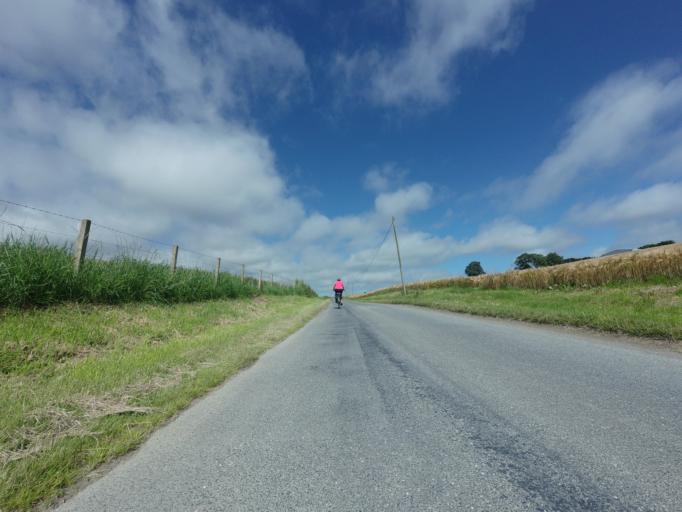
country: GB
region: Scotland
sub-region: Aberdeenshire
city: Turriff
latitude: 57.5661
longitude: -2.4937
